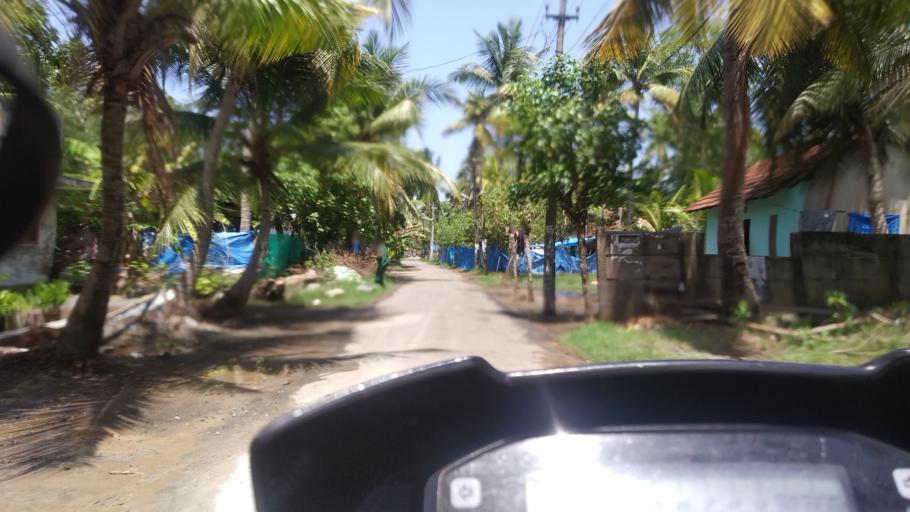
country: IN
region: Kerala
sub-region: Ernakulam
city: Elur
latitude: 10.0750
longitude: 76.2071
